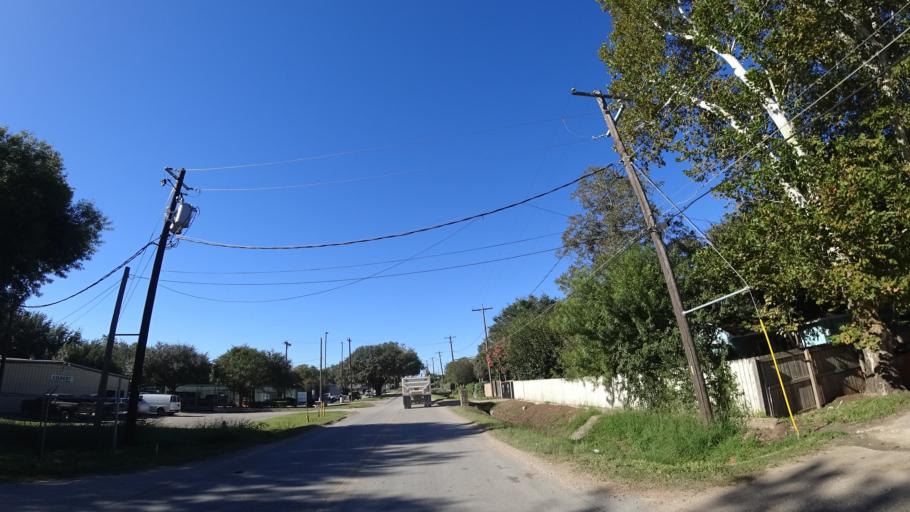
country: US
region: Texas
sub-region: Travis County
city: Austin
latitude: 30.2387
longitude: -97.6839
